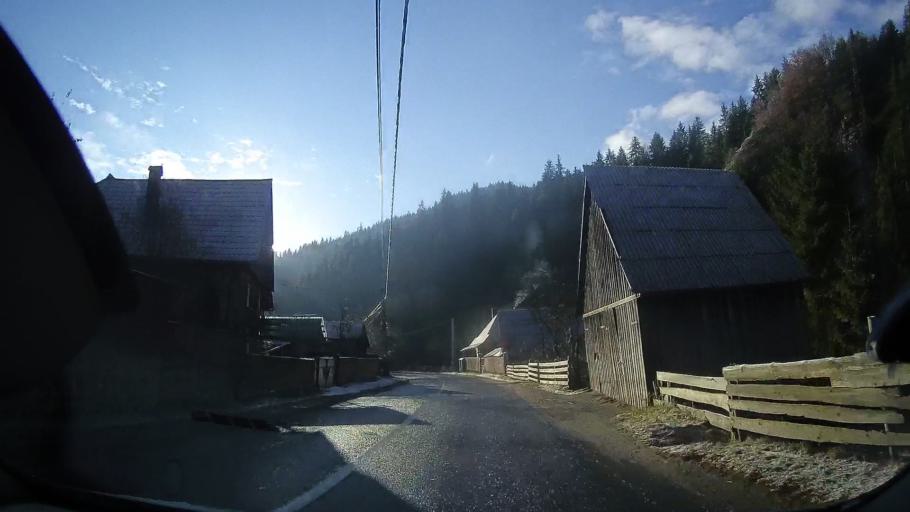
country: RO
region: Alba
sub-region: Comuna Scarisoara
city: Scarisoara
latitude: 46.4603
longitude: 22.8877
